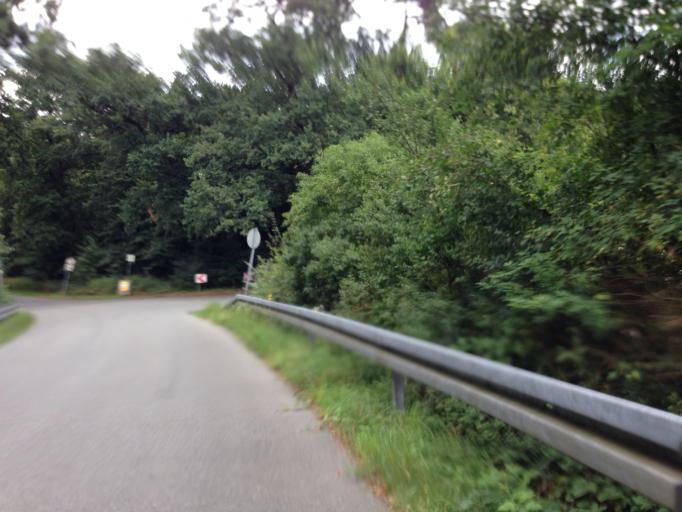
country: DE
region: Hesse
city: Obertshausen
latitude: 50.0701
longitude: 8.8838
